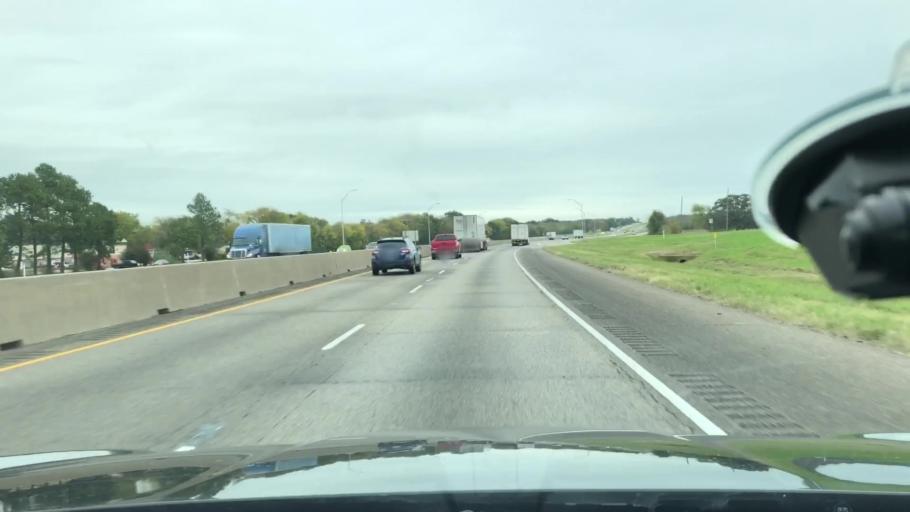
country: US
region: Texas
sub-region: Hopkins County
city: Sulphur Springs
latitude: 33.1442
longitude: -95.5628
